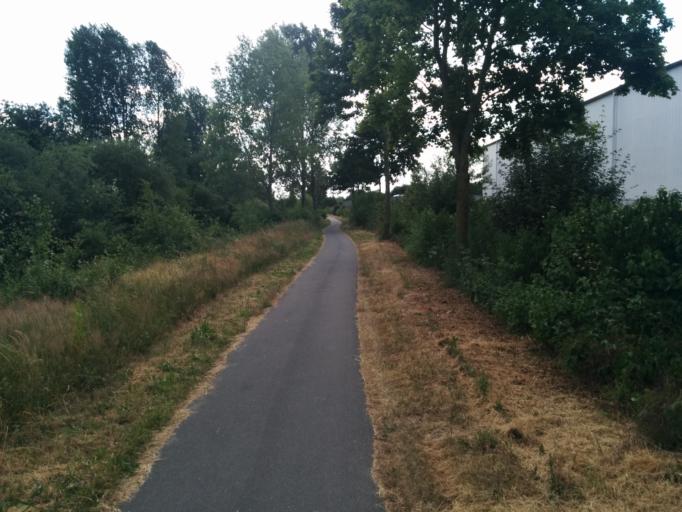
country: DE
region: Lower Saxony
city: Vechta
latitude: 52.7201
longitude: 8.2621
